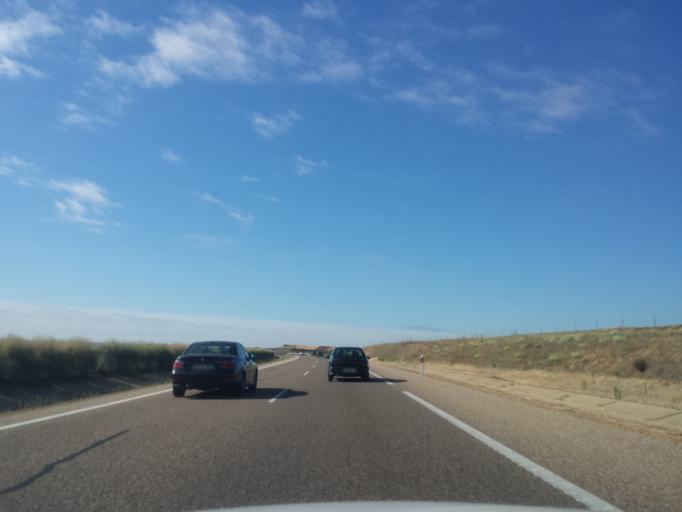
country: ES
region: Castille and Leon
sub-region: Provincia de Leon
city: Algadefe
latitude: 42.2200
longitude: -5.6000
